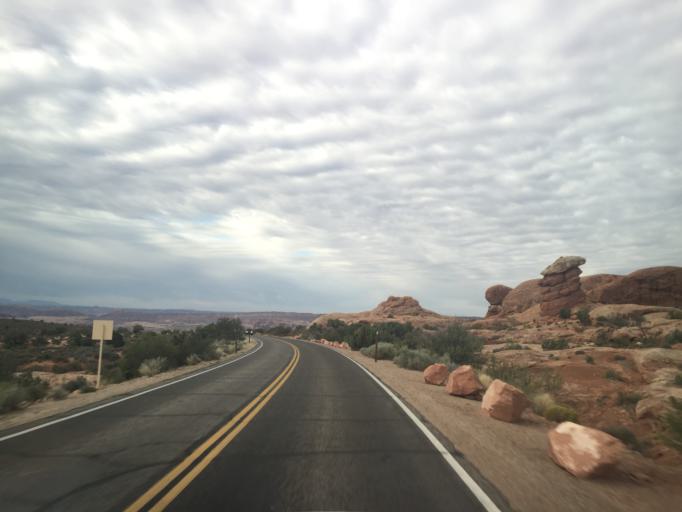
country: US
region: Utah
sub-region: Grand County
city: Moab
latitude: 38.6994
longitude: -109.5709
